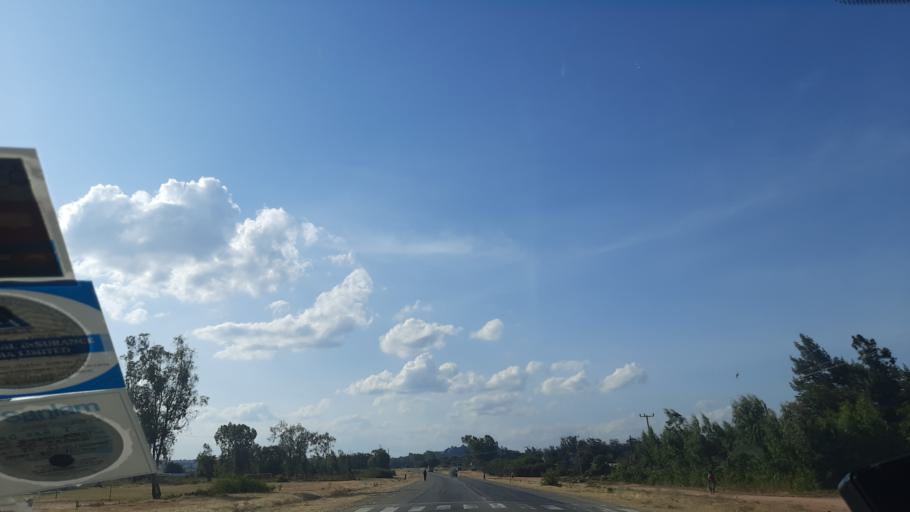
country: TZ
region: Singida
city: Puma
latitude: -5.0000
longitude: 34.7572
